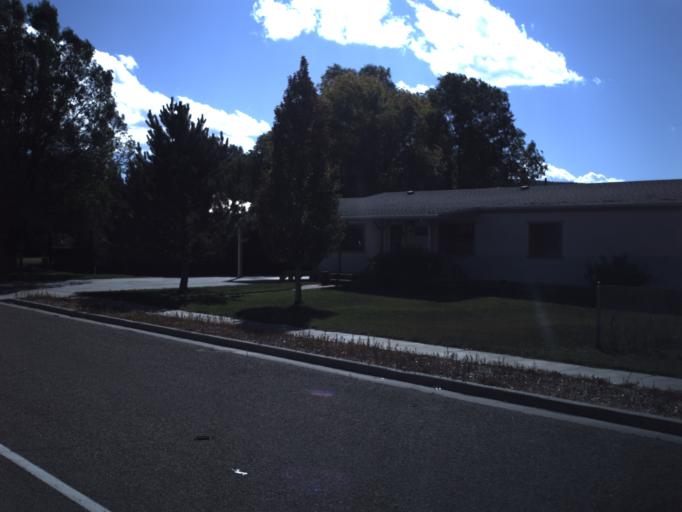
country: US
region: Utah
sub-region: Garfield County
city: Panguitch
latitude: 37.8177
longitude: -112.4356
